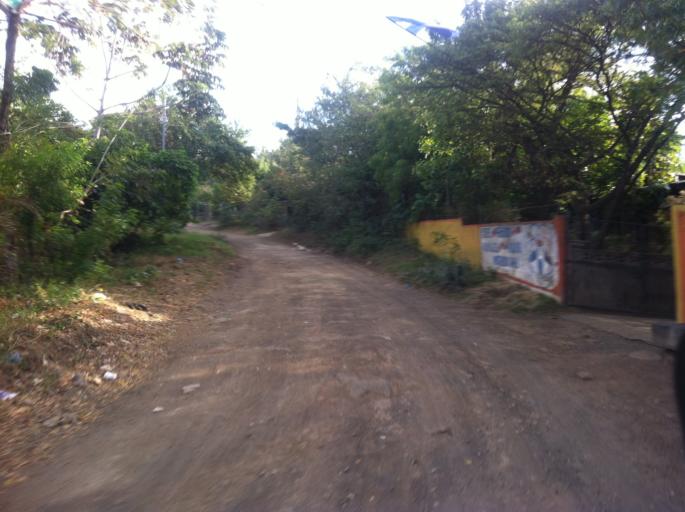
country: NI
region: Managua
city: Ciudad Sandino
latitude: 12.0938
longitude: -86.3136
